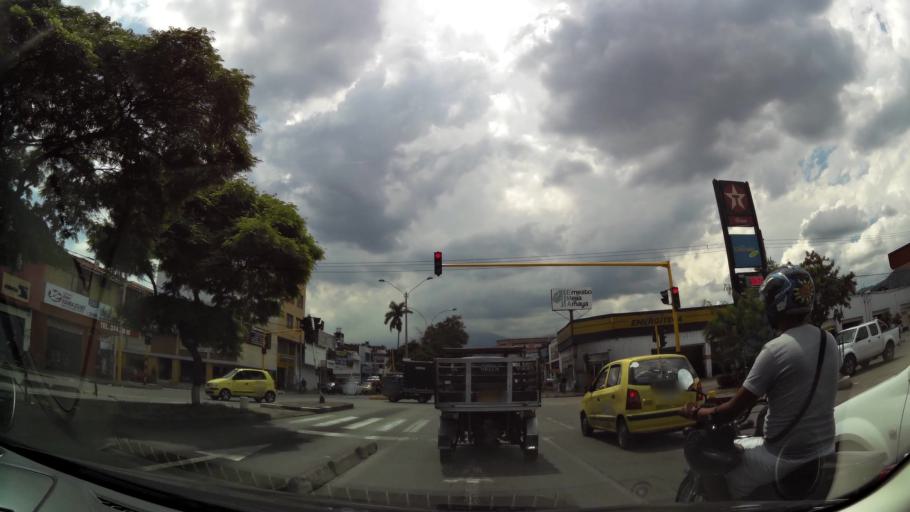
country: CO
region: Valle del Cauca
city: Cali
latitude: 3.4437
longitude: -76.5224
